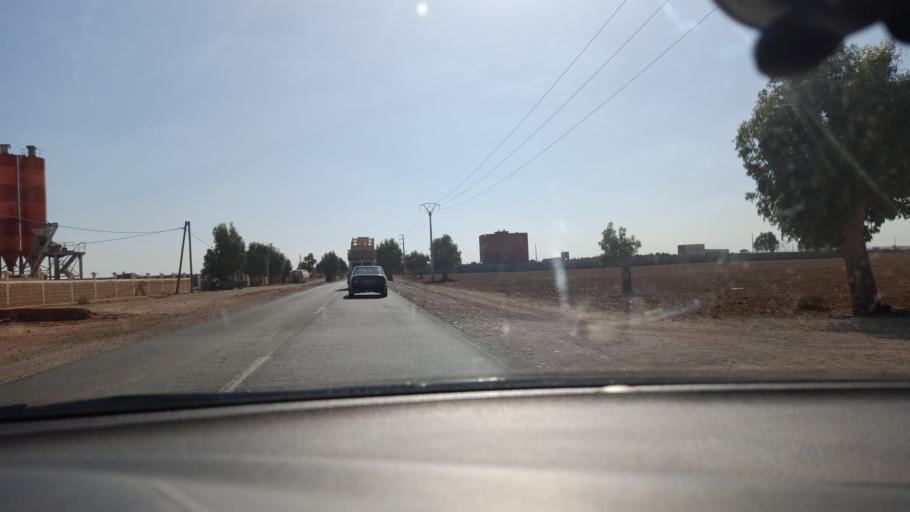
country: MA
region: Doukkala-Abda
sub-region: Safi
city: Youssoufia
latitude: 32.1025
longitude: -8.6120
